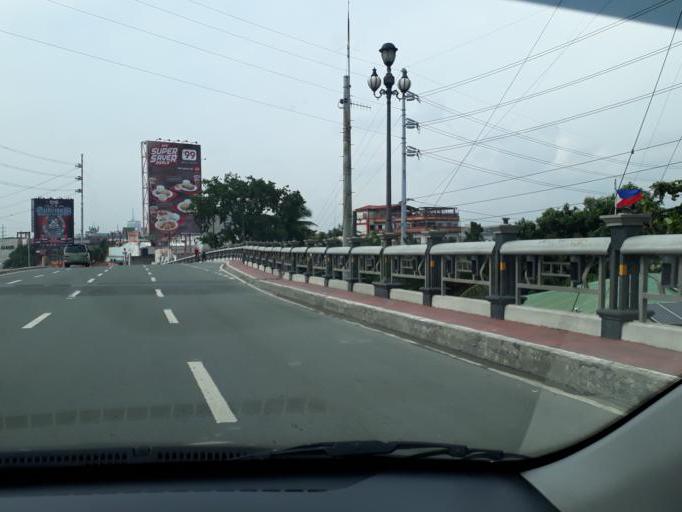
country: PH
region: Metro Manila
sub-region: City of Manila
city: Quiapo
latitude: 14.5962
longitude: 121.0015
